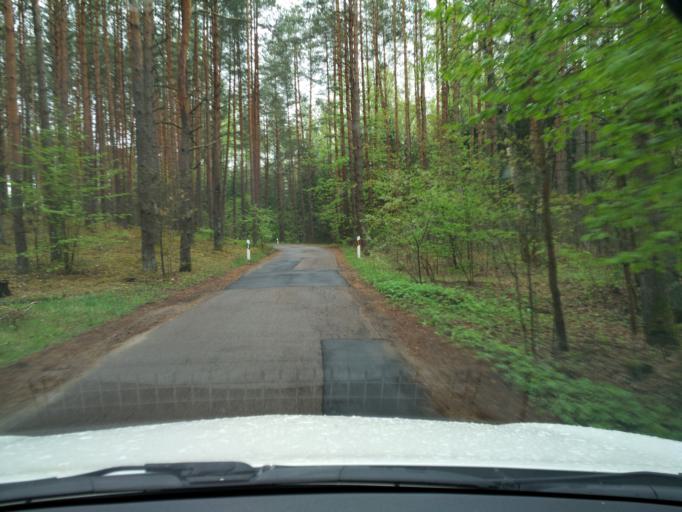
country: LT
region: Vilnius County
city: Rasos
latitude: 54.7407
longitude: 25.3979
